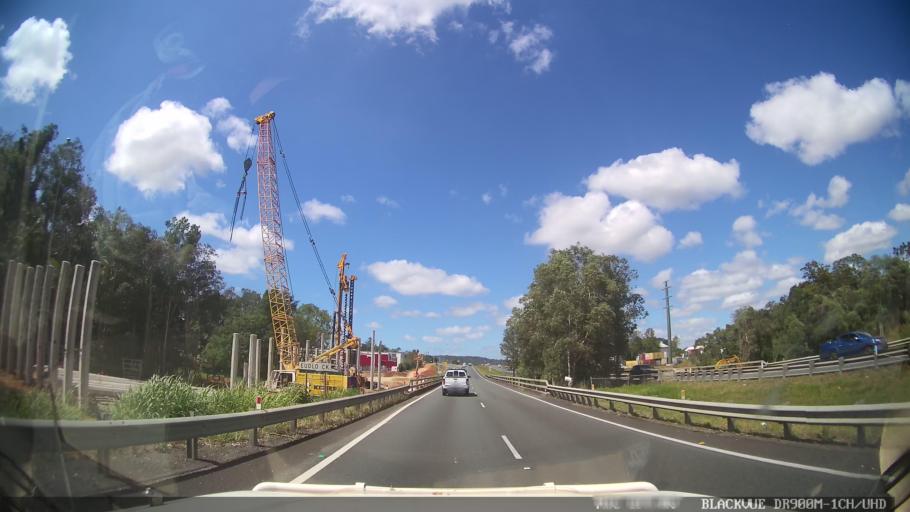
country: AU
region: Queensland
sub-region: Sunshine Coast
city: Woombye
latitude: -26.6807
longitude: 153.0028
